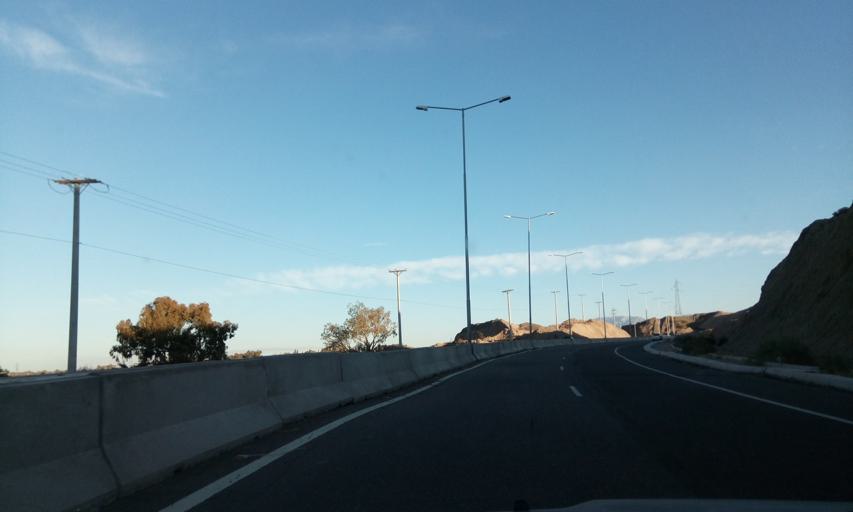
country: AR
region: San Juan
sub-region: Departamento de Rivadavia
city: Rivadavia
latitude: -31.4958
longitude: -68.6484
